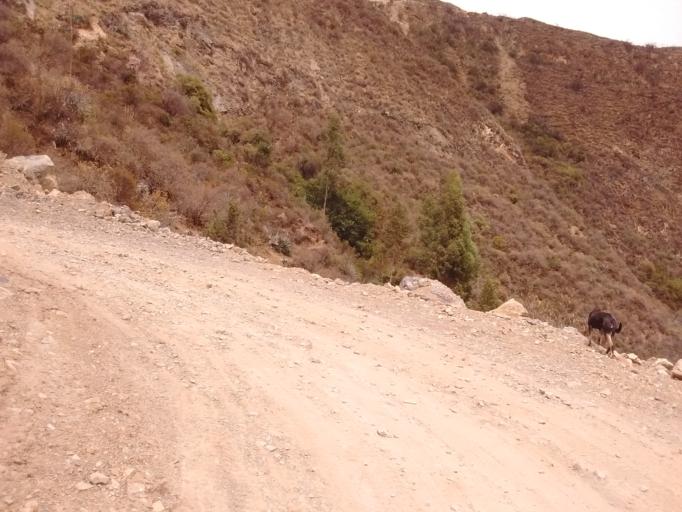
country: PE
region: Ayacucho
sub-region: Provincia de Victor Fajardo
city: Canaria
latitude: -13.8806
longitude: -73.9380
